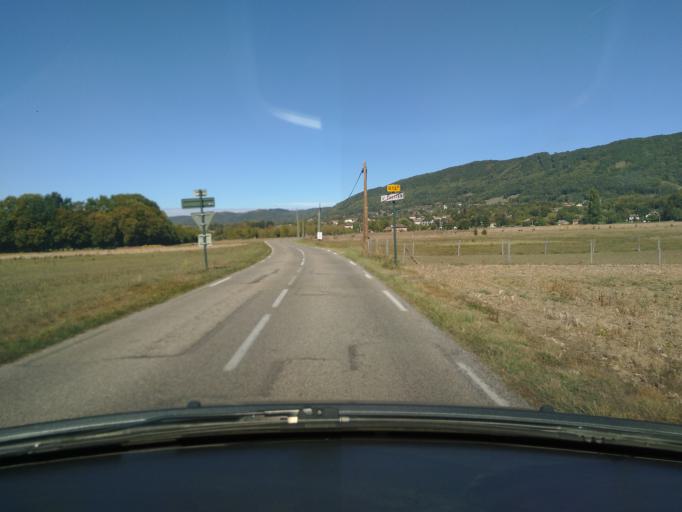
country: FR
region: Rhone-Alpes
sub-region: Departement de l'Isere
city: Saint-Cassien
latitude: 45.3616
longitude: 5.5552
